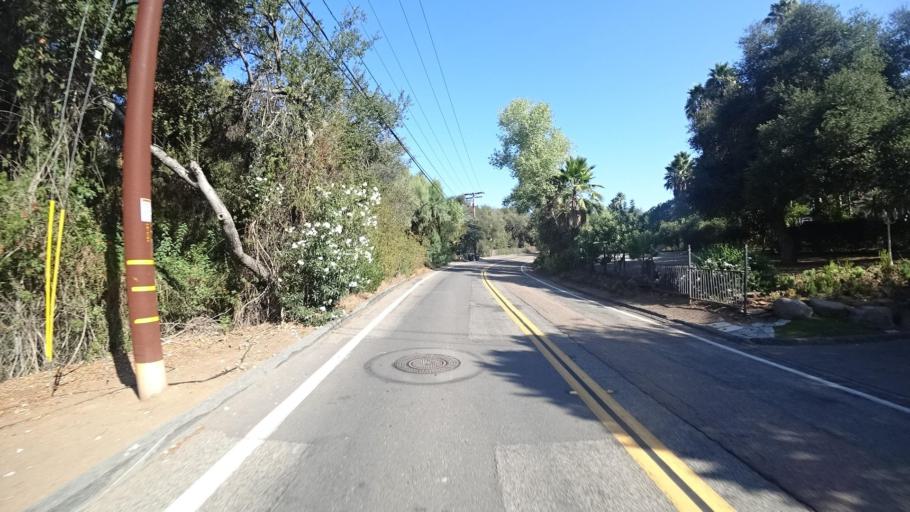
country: US
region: California
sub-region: San Diego County
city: Escondido
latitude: 33.0773
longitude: -117.0842
